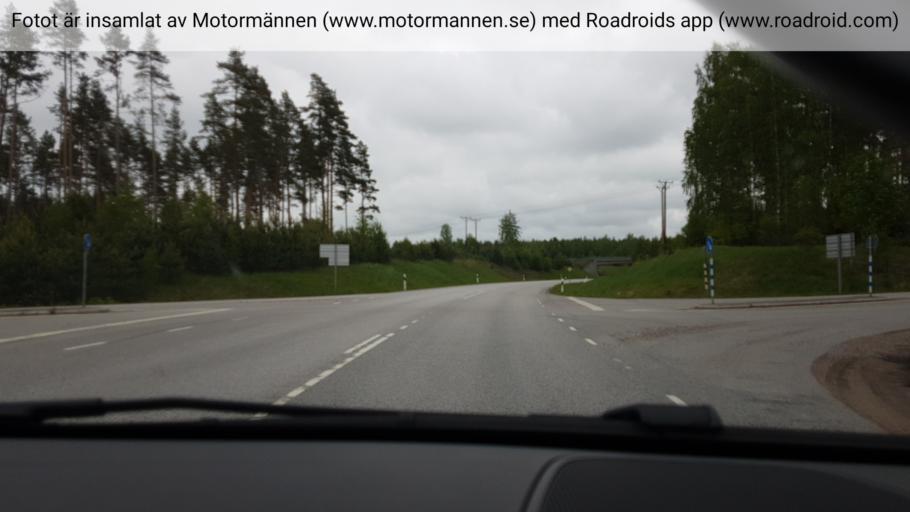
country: SE
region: Uppsala
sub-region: Osthammars Kommun
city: Bjorklinge
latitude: 60.0192
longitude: 17.5787
